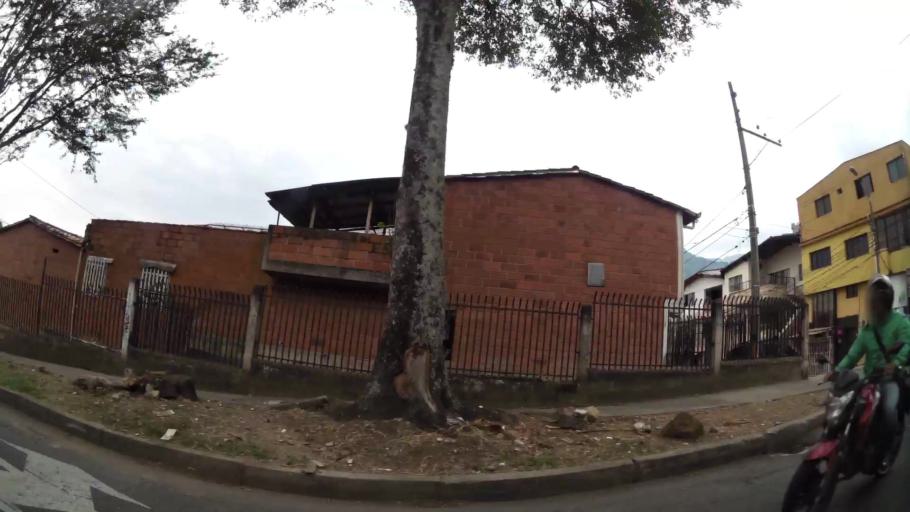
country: CO
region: Antioquia
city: Medellin
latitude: 6.2353
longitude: -75.5526
